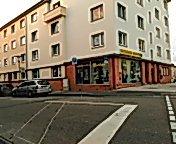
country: DE
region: Rheinland-Pfalz
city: Koblenz
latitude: 50.3607
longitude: 7.5818
